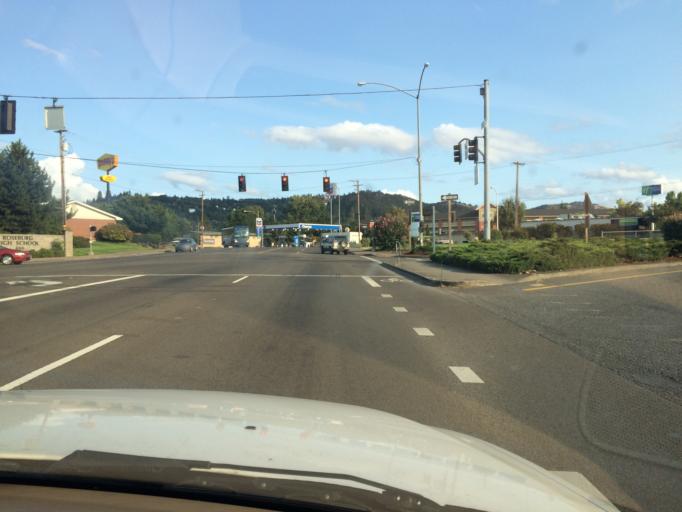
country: US
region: Oregon
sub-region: Douglas County
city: Roseburg
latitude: 43.2136
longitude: -123.3539
